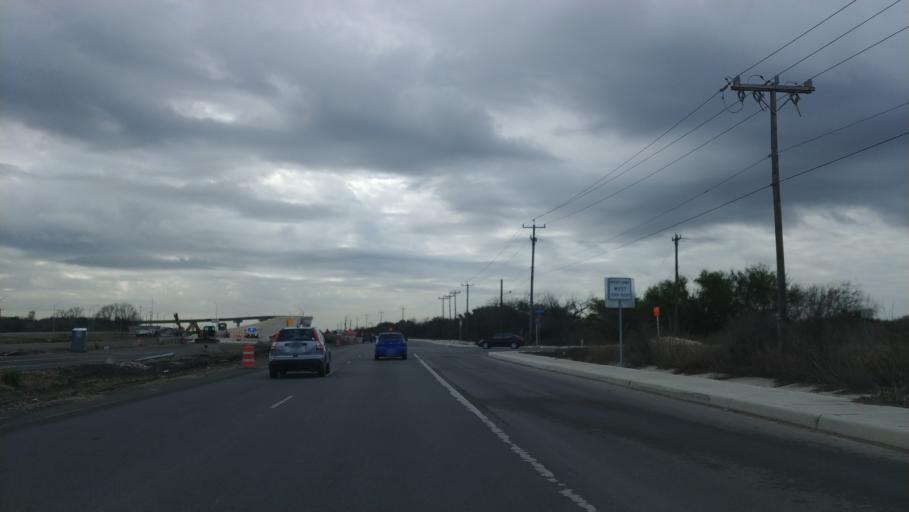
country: US
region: Texas
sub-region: Bexar County
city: Lackland Air Force Base
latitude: 29.3920
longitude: -98.7028
